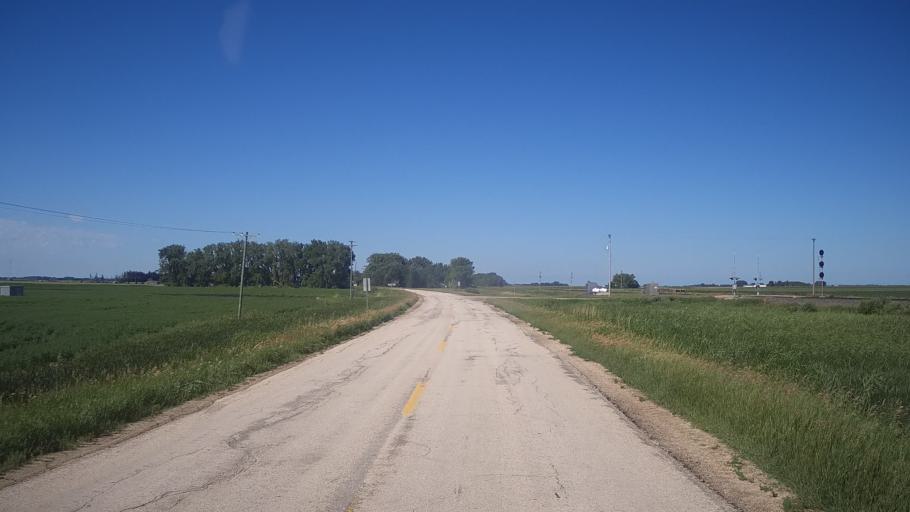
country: CA
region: Manitoba
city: Portage la Prairie
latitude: 50.0417
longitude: -98.0658
